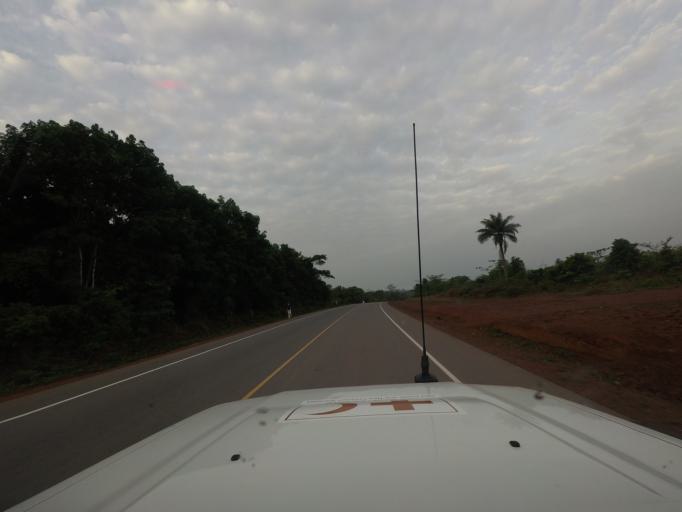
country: LR
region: Nimba
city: Sanniquellie
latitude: 7.1822
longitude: -9.0270
